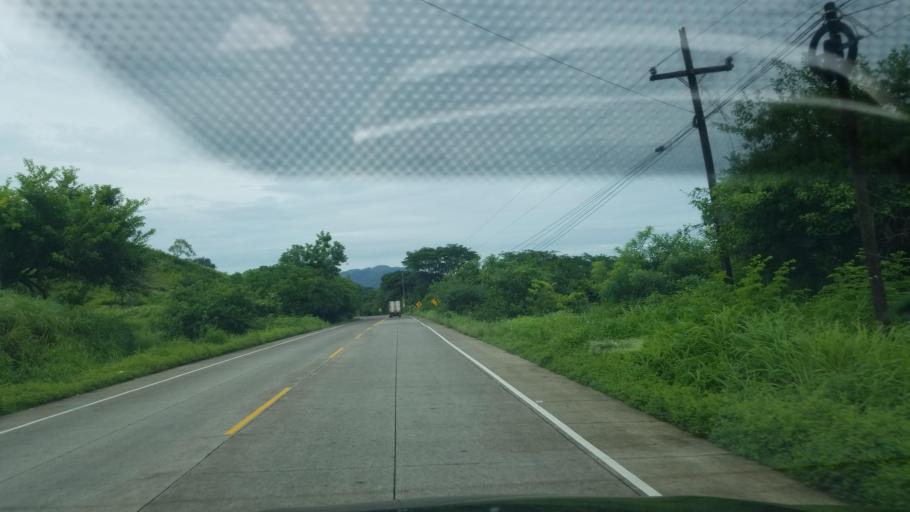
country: HN
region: Choluteca
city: Pespire
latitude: 13.6400
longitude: -87.3690
